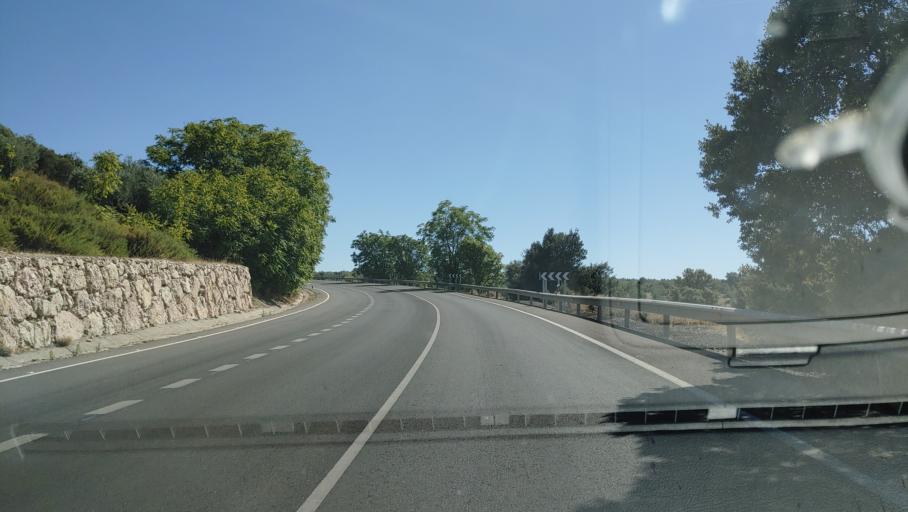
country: ES
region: Andalusia
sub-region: Provincia de Jaen
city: Campina
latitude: 38.2342
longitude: -2.9717
